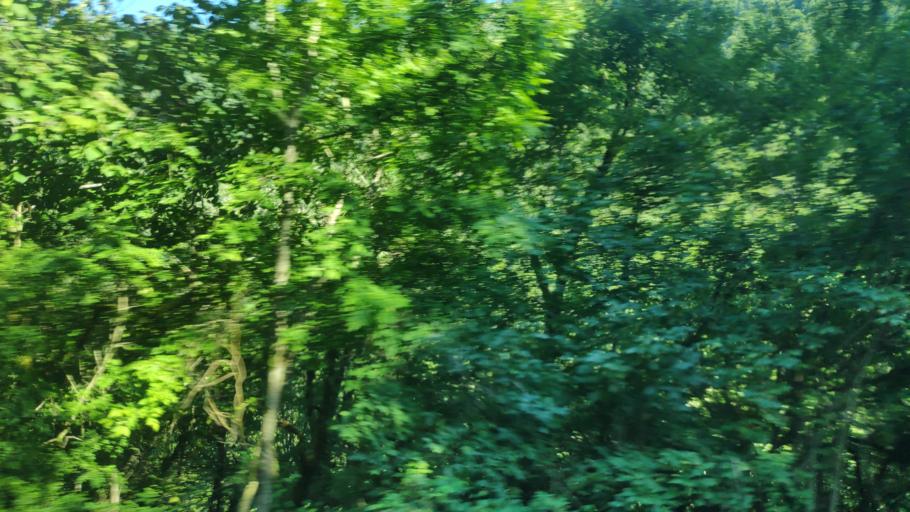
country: GE
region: Abkhazia
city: Gagra
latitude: 43.3541
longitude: 40.4208
